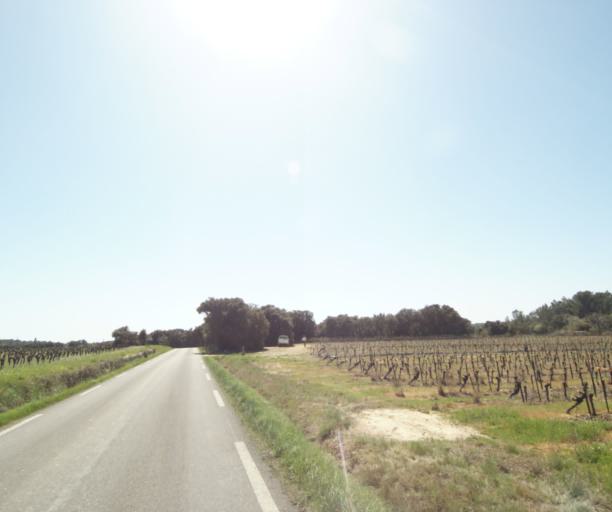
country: FR
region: Languedoc-Roussillon
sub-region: Departement de l'Herault
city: Beaulieu
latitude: 43.7319
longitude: 4.0095
